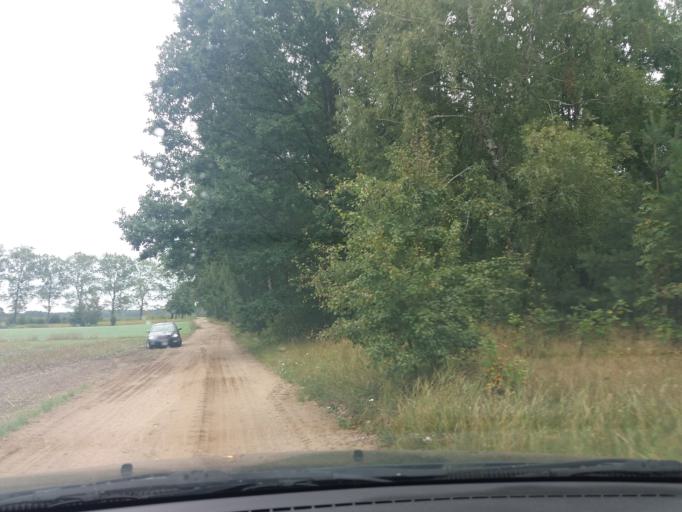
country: PL
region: Masovian Voivodeship
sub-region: Powiat mlawski
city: Wieczfnia Koscielna
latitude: 53.2341
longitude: 20.4869
